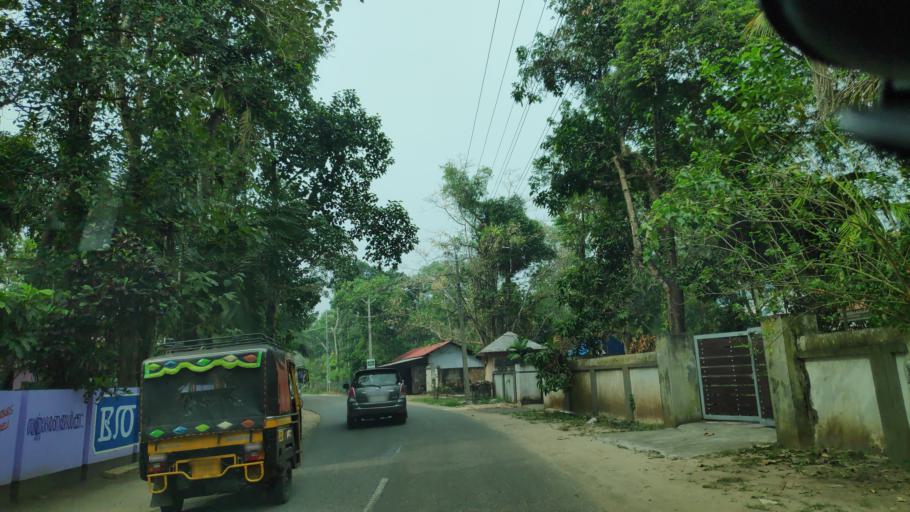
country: IN
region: Kerala
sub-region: Alappuzha
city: Alleppey
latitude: 9.5716
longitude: 76.3383
